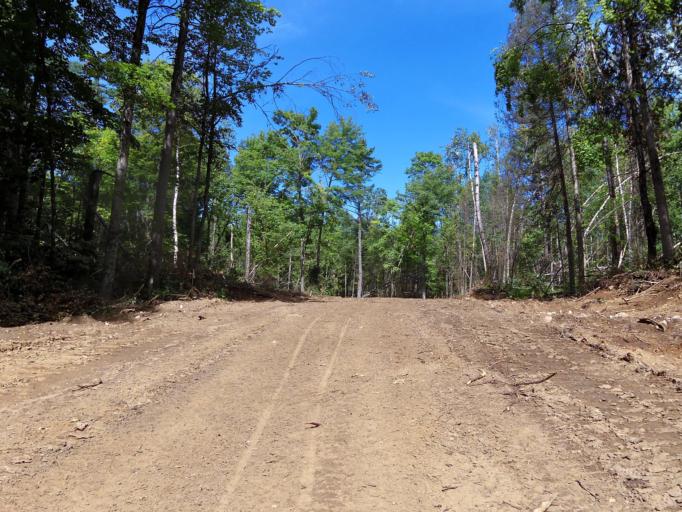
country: CA
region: Ontario
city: Renfrew
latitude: 45.1069
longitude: -76.7174
